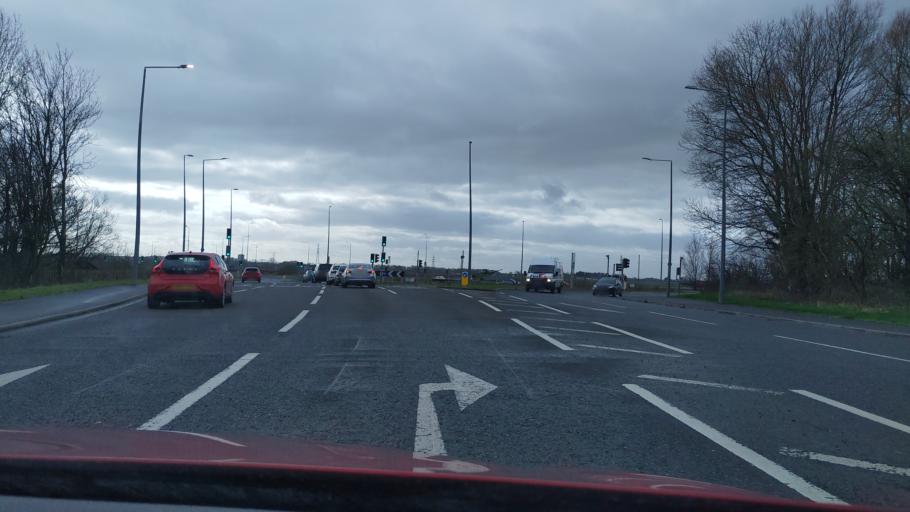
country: GB
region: England
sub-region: Lancashire
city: Leyland
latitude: 53.7144
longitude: -2.7142
